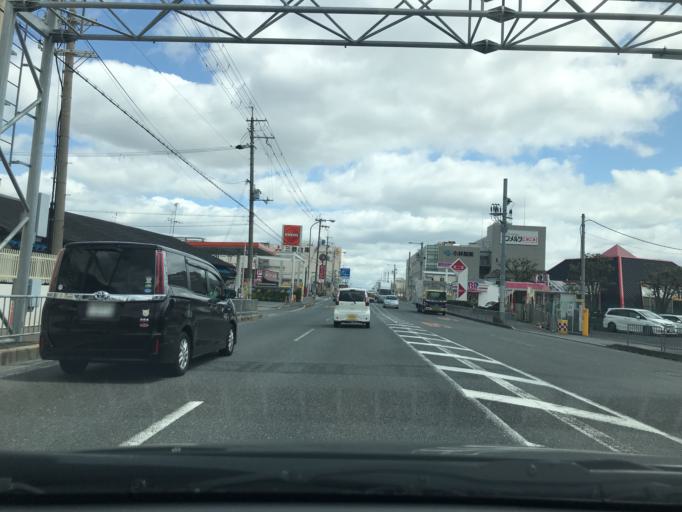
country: JP
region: Osaka
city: Ibaraki
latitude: 34.8363
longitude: 135.5336
